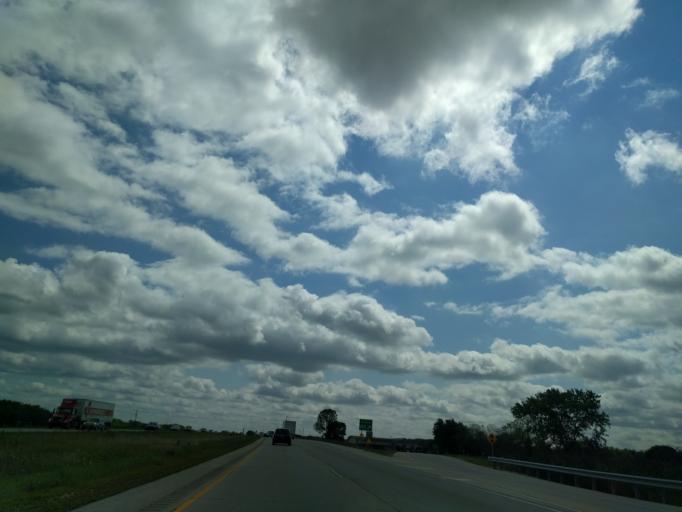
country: US
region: Wisconsin
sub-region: Milwaukee County
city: Bayside
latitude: 43.2237
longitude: -87.9214
